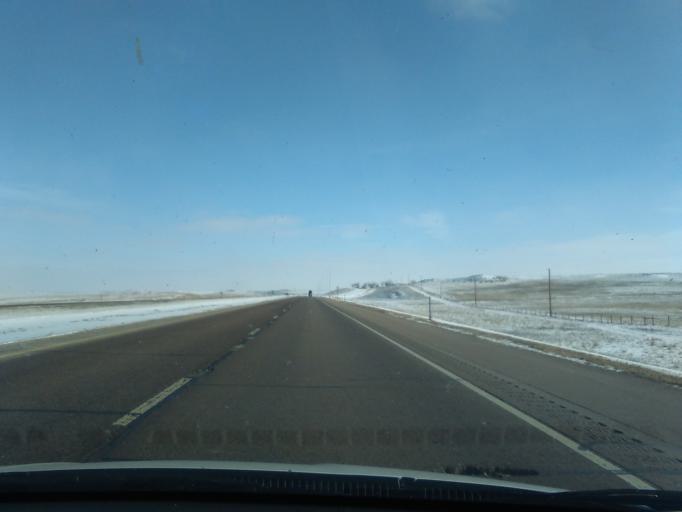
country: US
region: Wyoming
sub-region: Laramie County
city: Pine Bluffs
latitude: 41.1916
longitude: -103.8789
